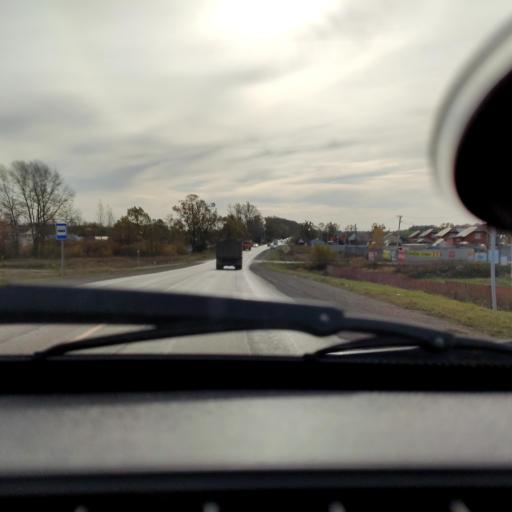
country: RU
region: Bashkortostan
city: Avdon
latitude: 54.7381
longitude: 55.8015
